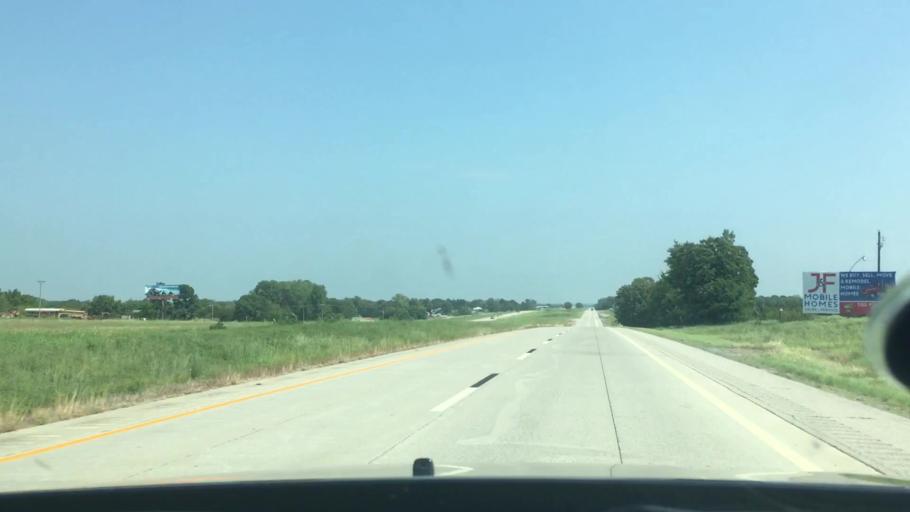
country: US
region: Oklahoma
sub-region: Atoka County
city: Atoka
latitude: 34.1963
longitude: -96.2400
